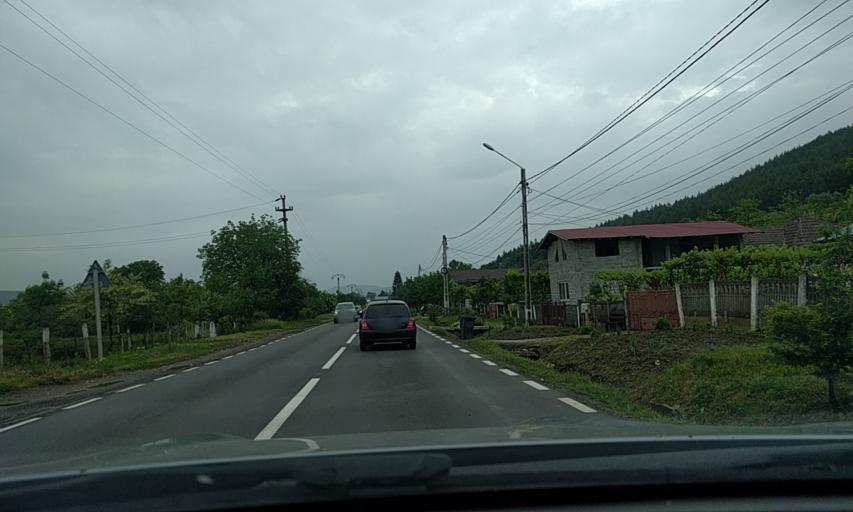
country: RO
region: Dambovita
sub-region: Comuna Vulcana-Pandele
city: Vulcana-Pandele
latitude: 45.0087
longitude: 25.4020
